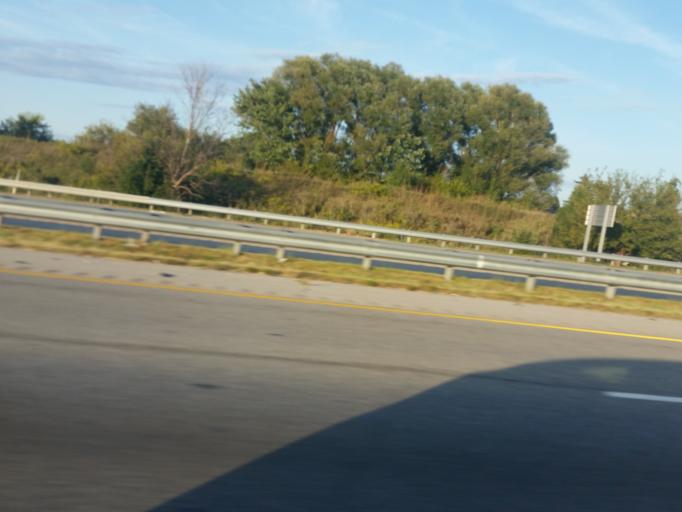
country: US
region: Indiana
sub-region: Boone County
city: Whitestown
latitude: 39.9411
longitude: -86.3478
